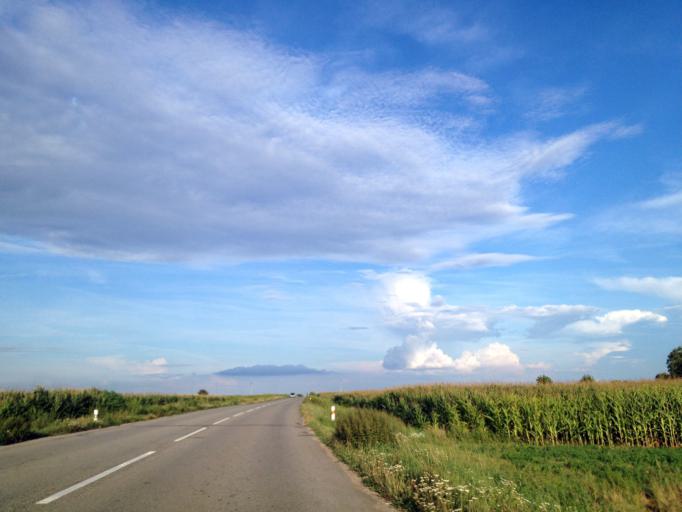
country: SK
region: Nitriansky
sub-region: Okres Komarno
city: Hurbanovo
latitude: 47.9109
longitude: 18.3119
